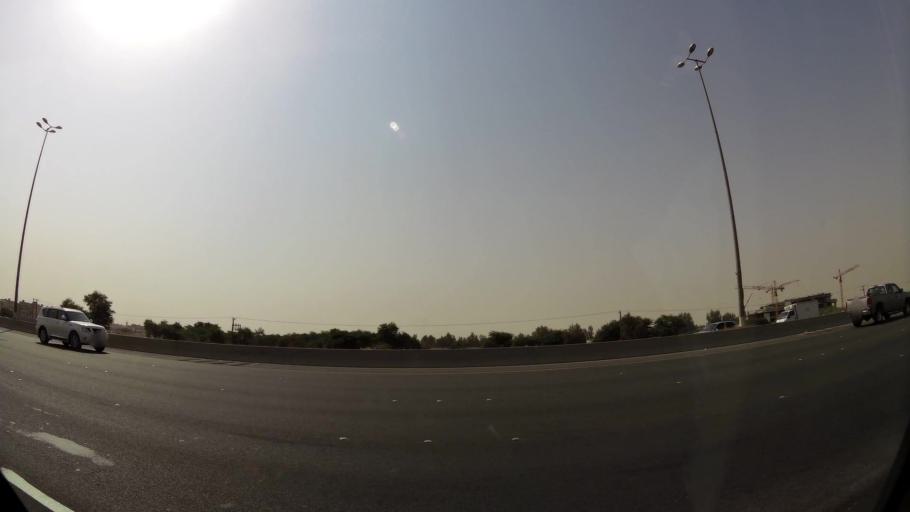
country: KW
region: Muhafazat al Jahra'
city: Al Jahra'
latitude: 29.3315
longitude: 47.7339
